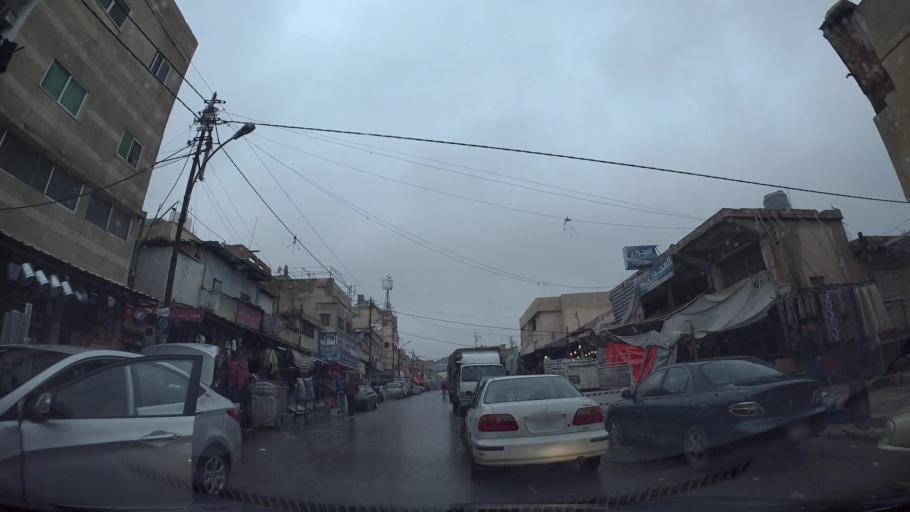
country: JO
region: Amman
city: Amman
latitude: 31.9653
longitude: 35.9259
